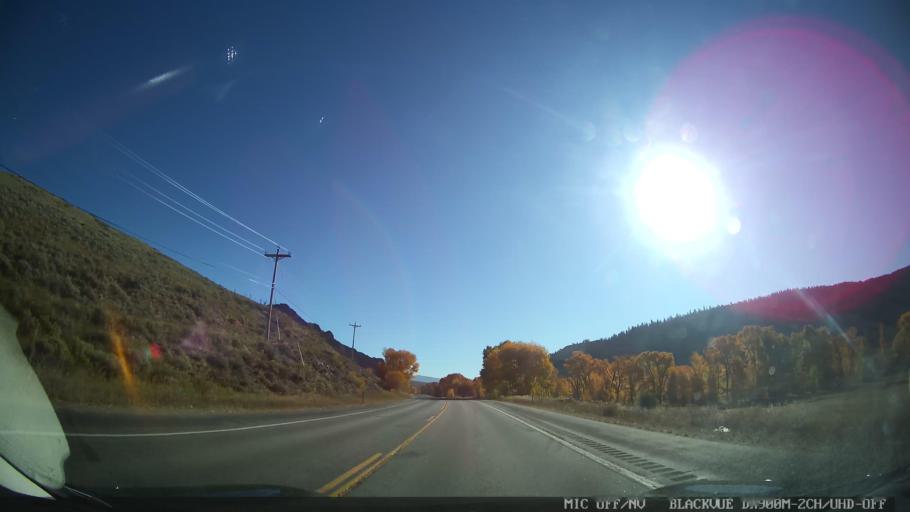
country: US
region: Colorado
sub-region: Grand County
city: Granby
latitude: 40.1082
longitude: -106.0119
